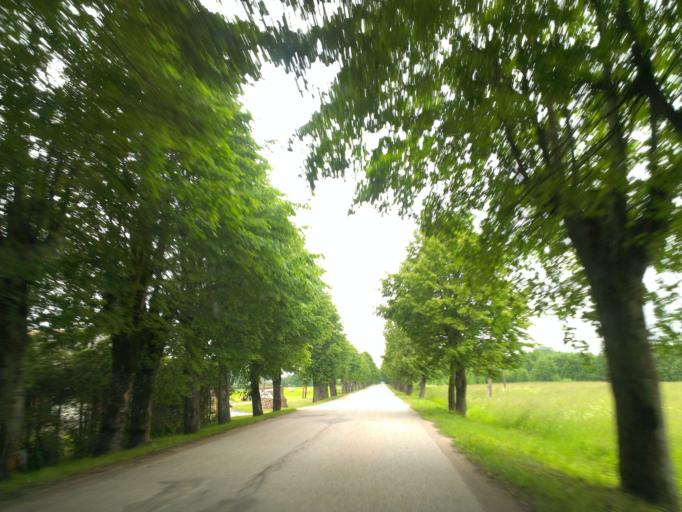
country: LV
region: Durbe
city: Liegi
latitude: 56.7302
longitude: 21.4013
